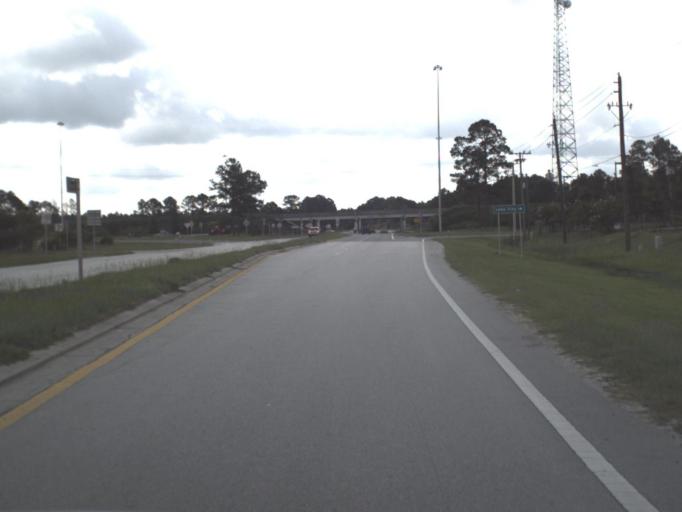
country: US
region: Florida
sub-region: Baker County
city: Macclenny
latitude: 30.2644
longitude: -82.1071
